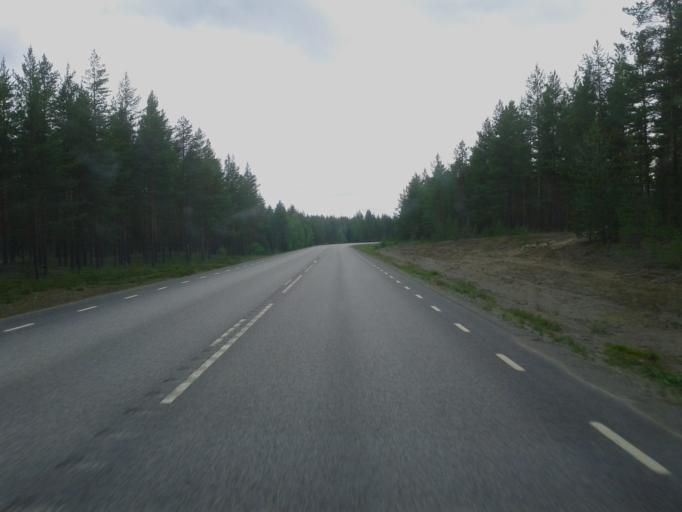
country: SE
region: Vaesterbotten
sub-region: Skelleftea Kommun
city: Langsele
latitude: 64.9342
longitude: 19.9555
